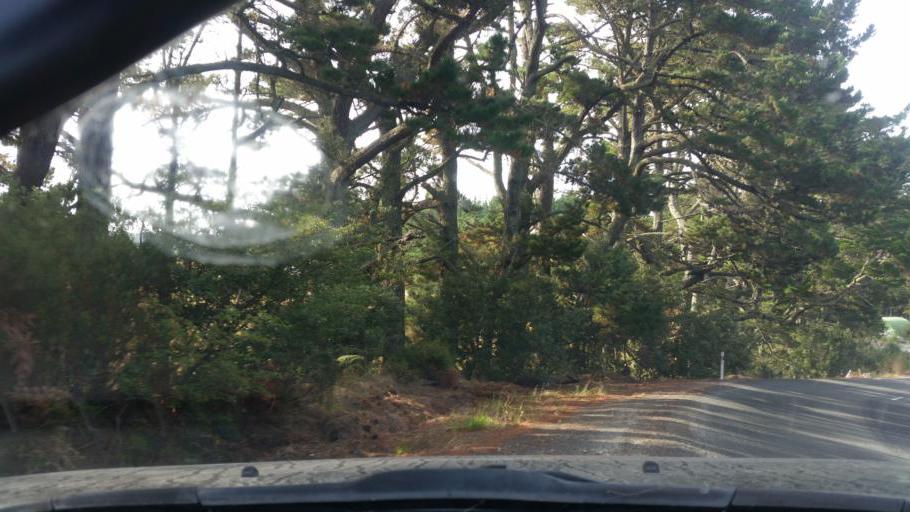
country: NZ
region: Northland
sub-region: Kaipara District
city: Dargaville
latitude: -36.2178
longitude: 174.0369
